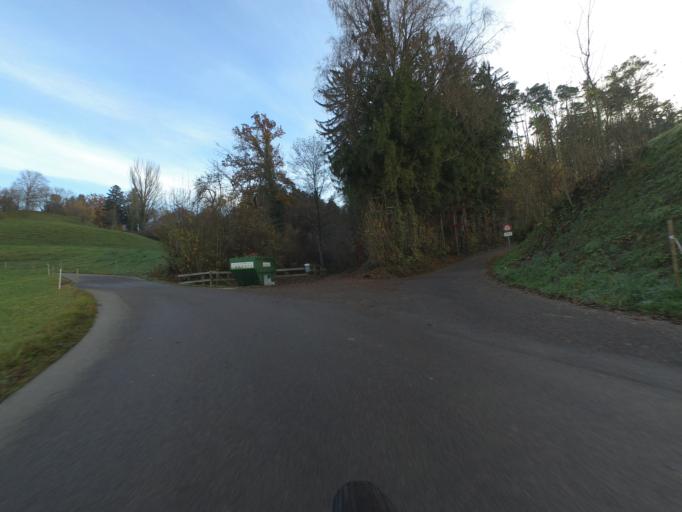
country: CH
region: Thurgau
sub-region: Frauenfeld District
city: Pfyn
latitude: 47.5700
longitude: 8.9427
